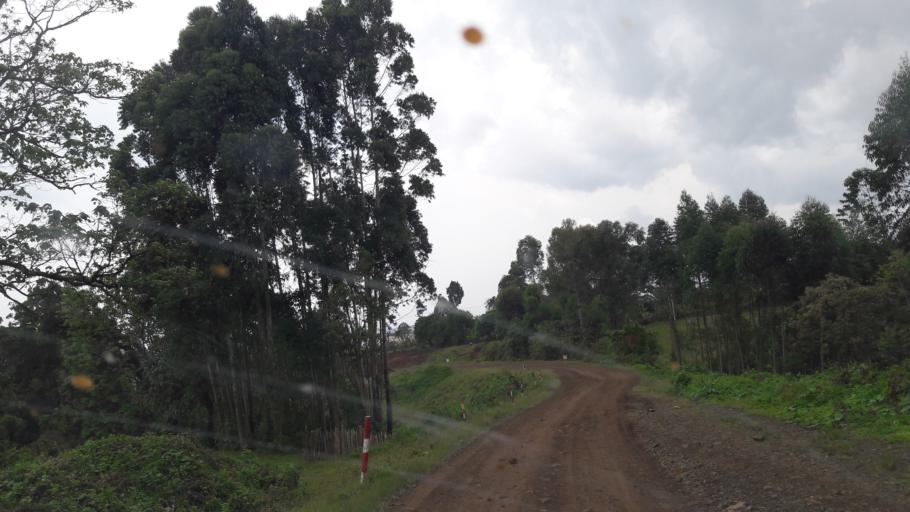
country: ET
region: Southern Nations, Nationalities, and People's Region
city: Tippi
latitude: 7.6476
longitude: 35.5057
